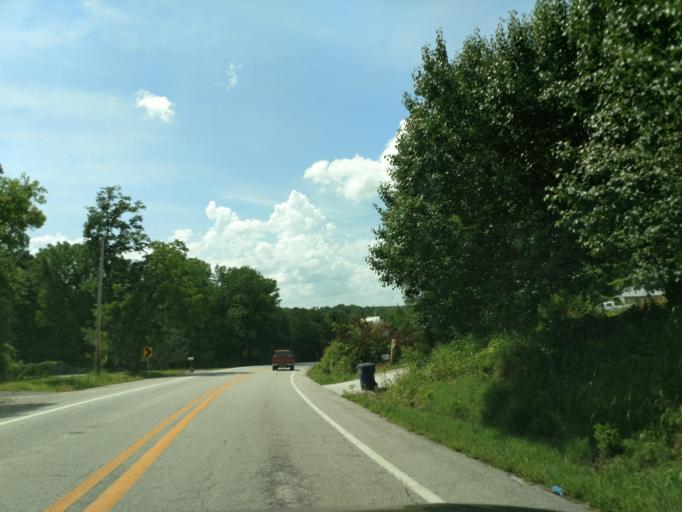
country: US
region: Arkansas
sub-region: Boone County
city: Harrison
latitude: 36.2892
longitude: -93.2375
